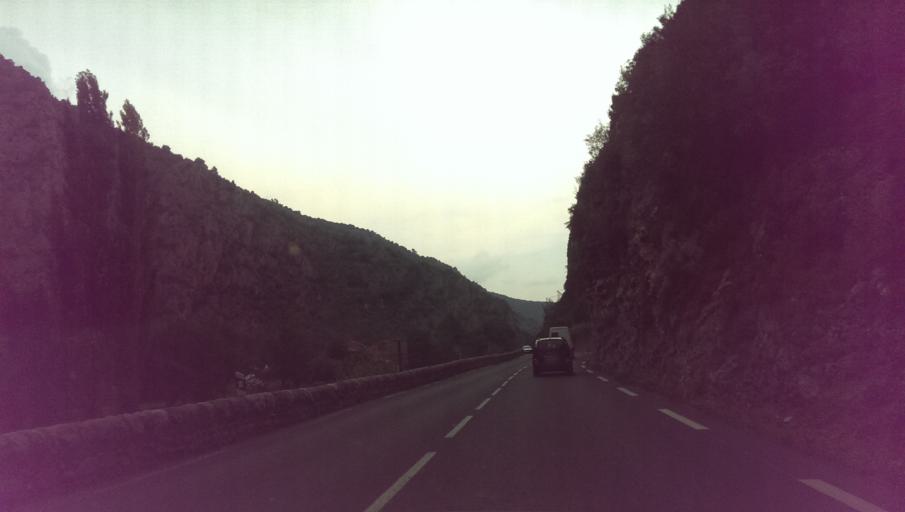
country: FR
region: Languedoc-Roussillon
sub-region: Departement des Pyrenees-Orientales
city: Ria-Sirach
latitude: 42.5917
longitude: 2.3717
